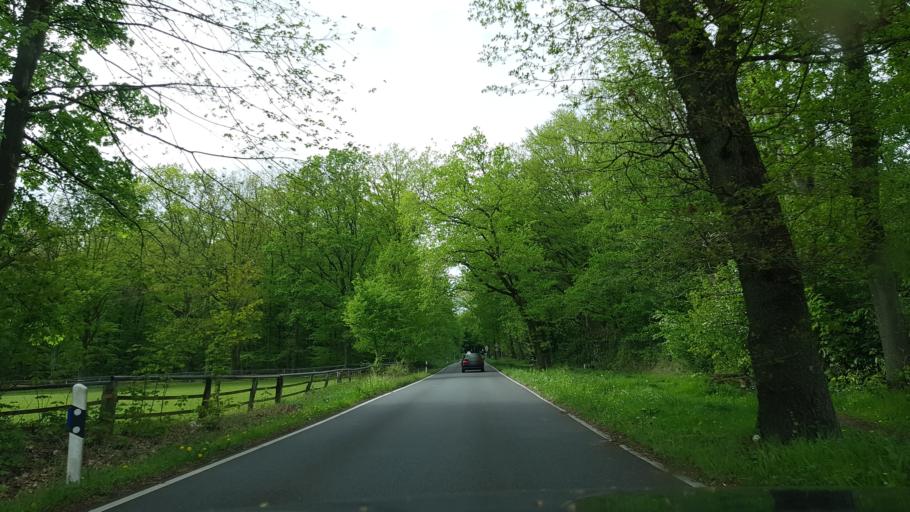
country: DE
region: North Rhine-Westphalia
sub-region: Regierungsbezirk Dusseldorf
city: Muelheim (Ruhr)
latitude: 51.3861
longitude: 6.8355
